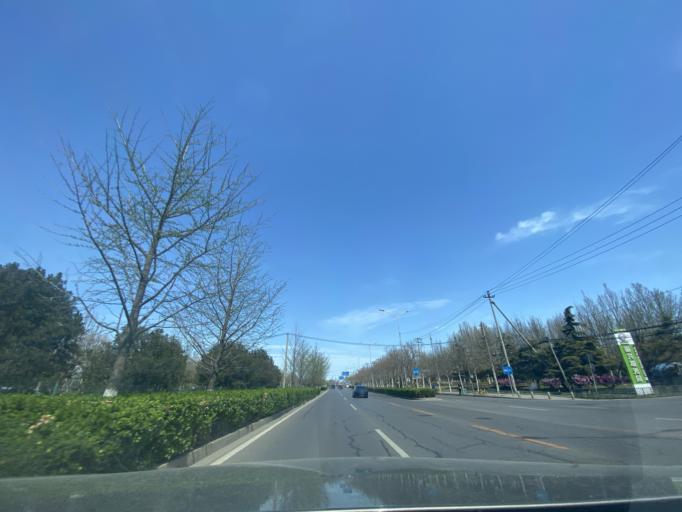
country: CN
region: Beijing
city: Sijiqing
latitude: 39.9430
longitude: 116.2408
